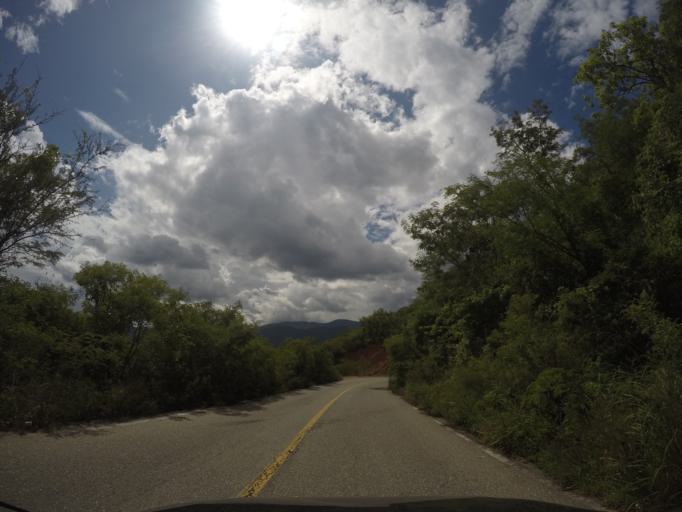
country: MX
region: Oaxaca
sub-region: San Jeronimo Coatlan
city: San Cristobal Honduras
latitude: 16.4328
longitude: -97.0478
